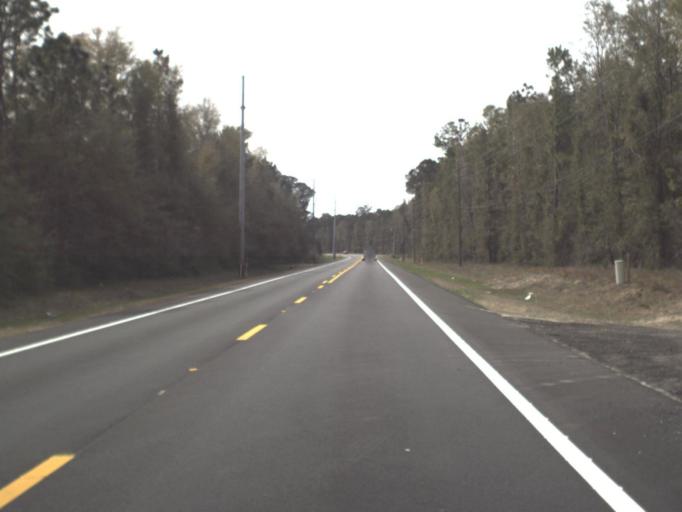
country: US
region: Florida
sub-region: Gadsden County
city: Midway
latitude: 30.4033
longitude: -84.5795
